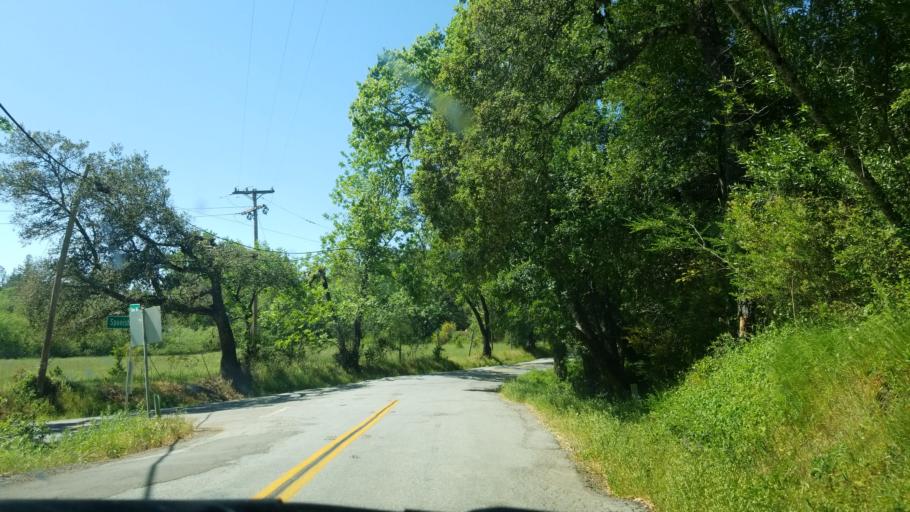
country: US
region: California
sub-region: Santa Cruz County
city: Day Valley
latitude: 37.1053
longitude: -121.8998
